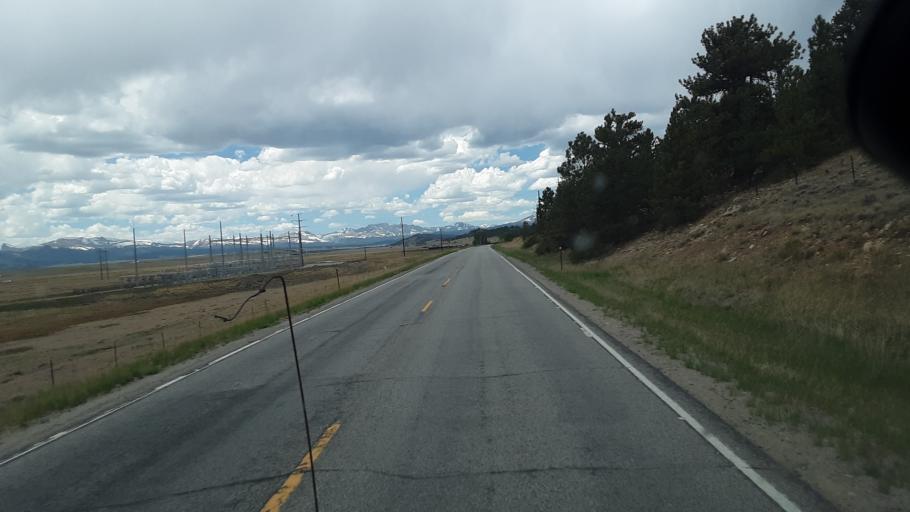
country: US
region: Colorado
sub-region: Park County
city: Fairplay
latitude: 39.0745
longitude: -105.8618
